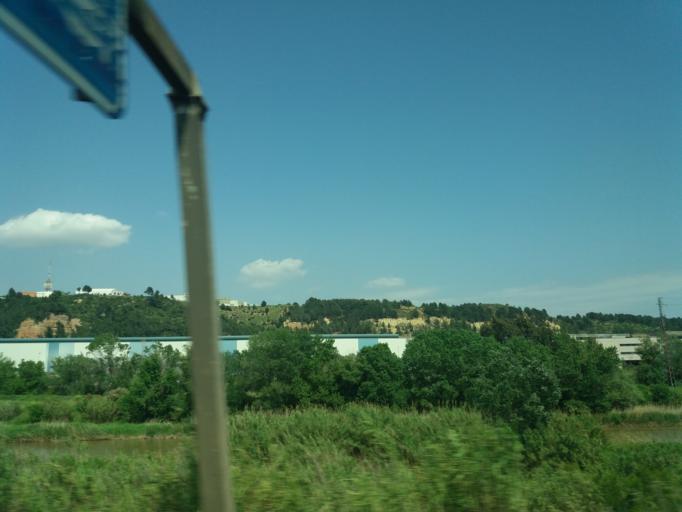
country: ES
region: Catalonia
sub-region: Provincia de Barcelona
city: Sant Andreu de la Barca
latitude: 41.4568
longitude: 1.9754
